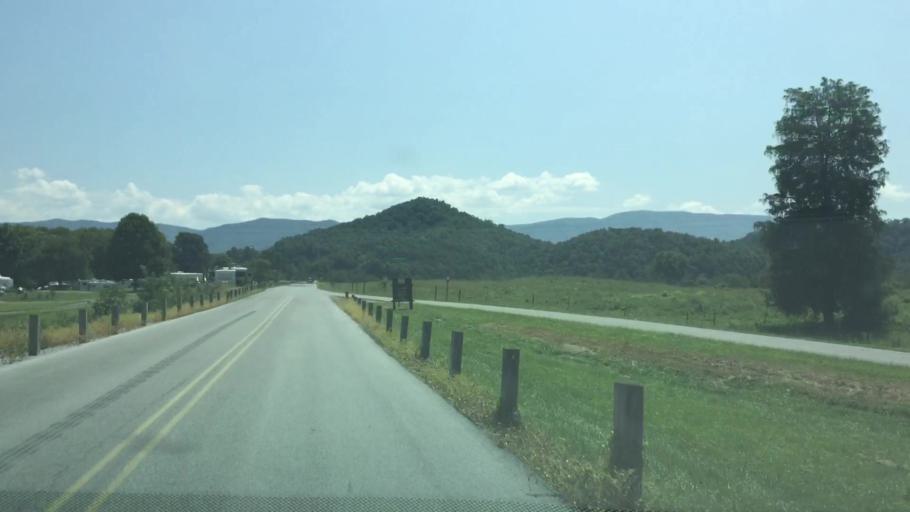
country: US
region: Tennessee
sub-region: Sullivan County
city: Fairmount
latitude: 36.5821
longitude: -82.0508
